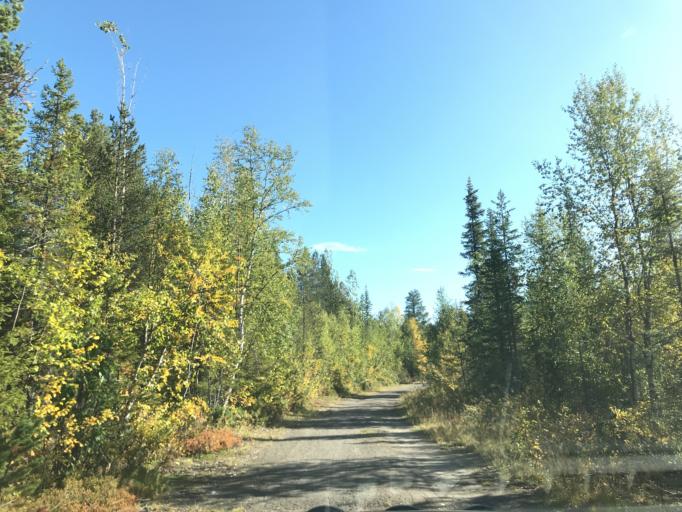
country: SE
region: Norrbotten
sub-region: Gallivare Kommun
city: Malmberget
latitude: 67.6470
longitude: 21.0996
